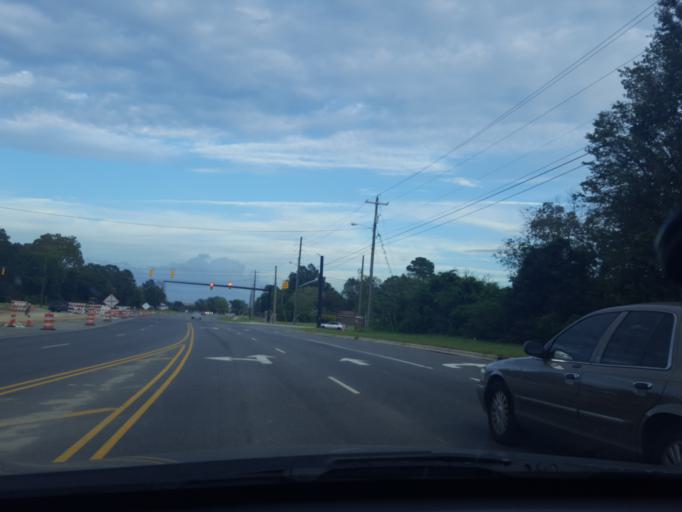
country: US
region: North Carolina
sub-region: Pitt County
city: Greenville
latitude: 35.6078
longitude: -77.3925
